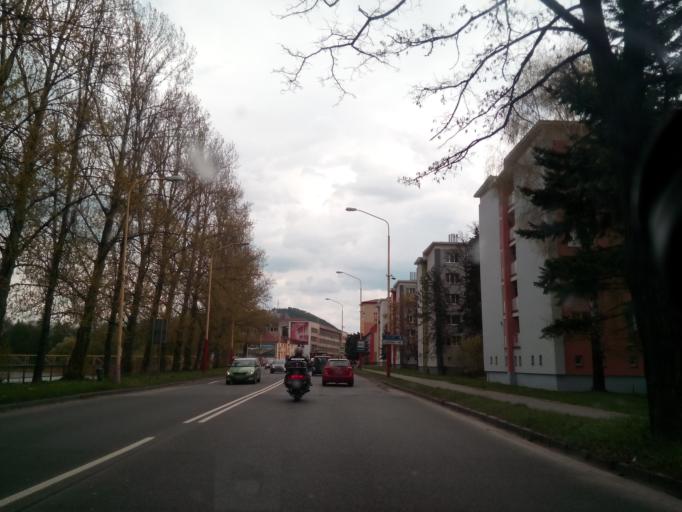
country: SK
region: Zilinsky
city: Ruzomberok
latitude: 49.0842
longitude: 19.2897
